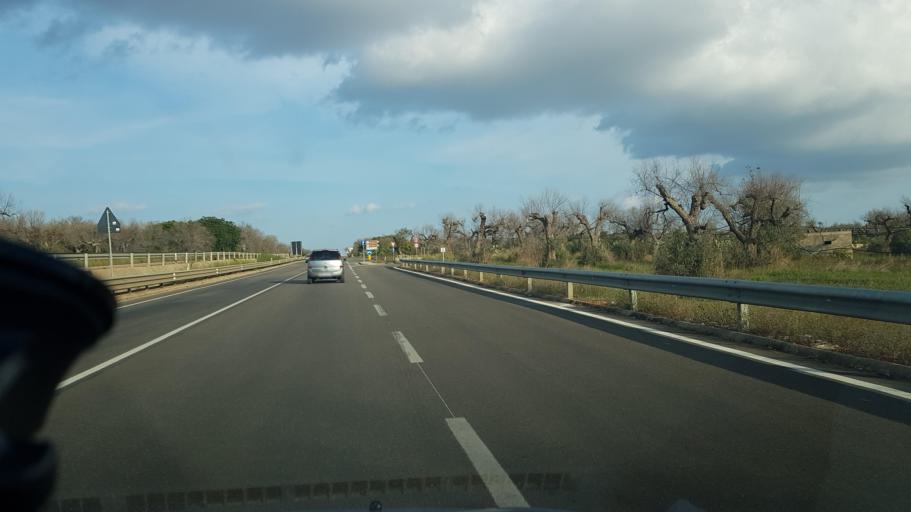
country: IT
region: Apulia
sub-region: Provincia di Lecce
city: Acquarica del Capo
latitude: 39.9177
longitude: 18.2184
